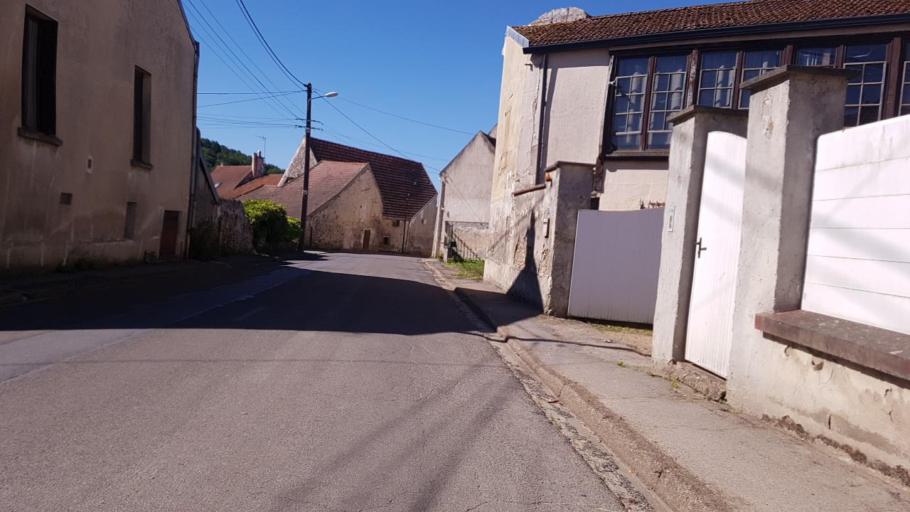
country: FR
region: Picardie
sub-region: Departement de l'Aisne
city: Chezy-sur-Marne
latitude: 48.9769
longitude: 3.3370
